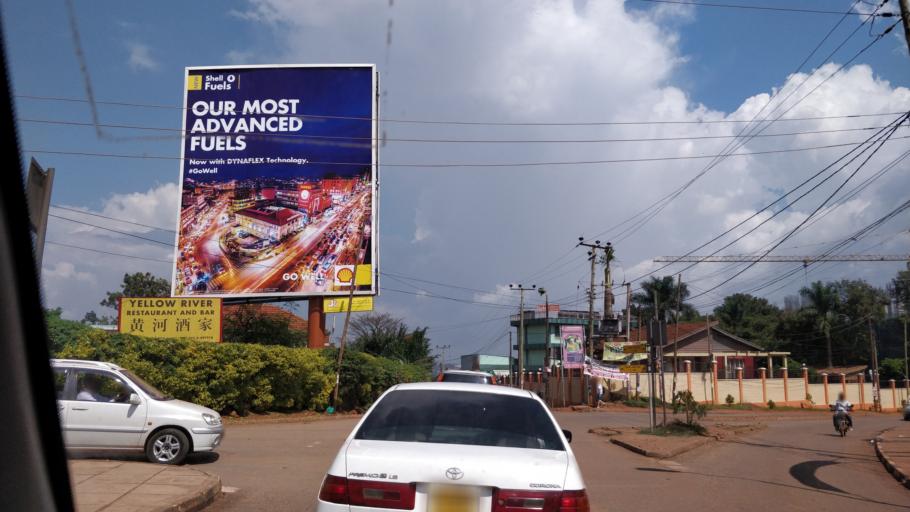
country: UG
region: Central Region
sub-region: Kampala District
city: Kampala
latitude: 0.3001
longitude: 32.6070
